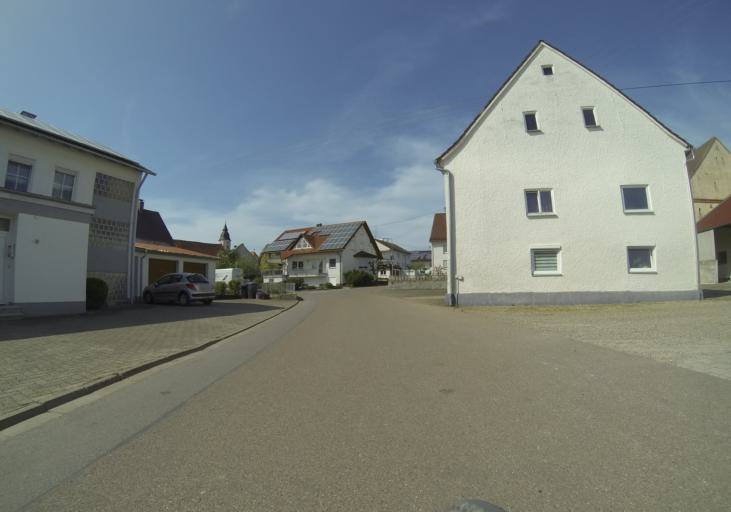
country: DE
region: Baden-Wuerttemberg
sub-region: Tuebingen Region
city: Huttisheim
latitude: 48.2599
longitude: 9.9270
